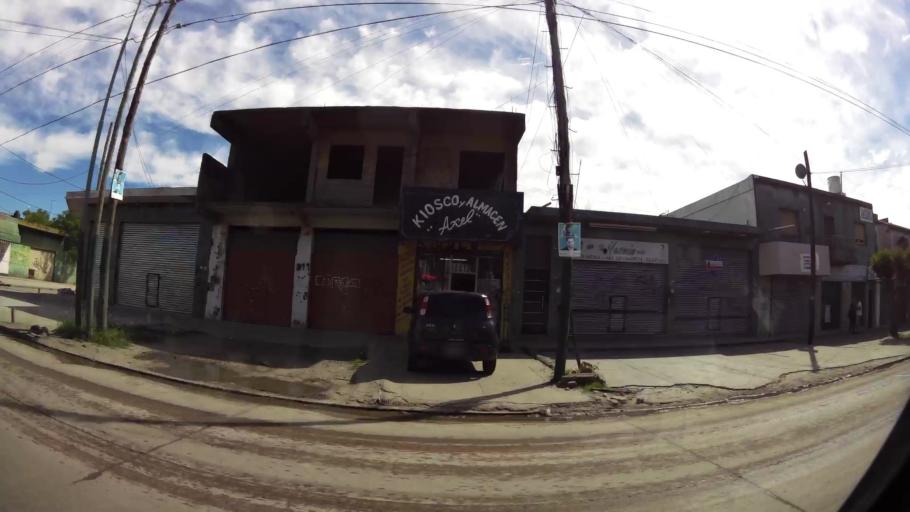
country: AR
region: Buenos Aires
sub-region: Partido de Almirante Brown
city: Adrogue
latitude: -34.7901
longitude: -58.3122
